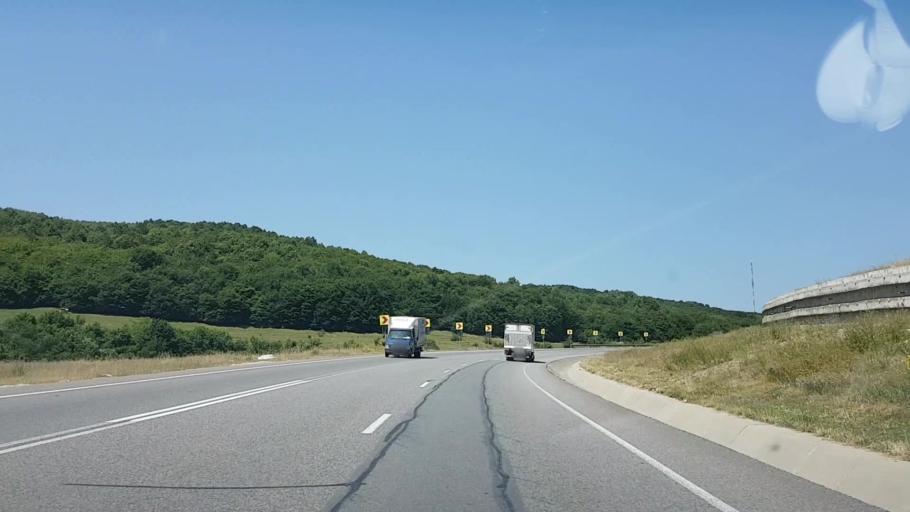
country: RO
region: Cluj
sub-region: Comuna Feleacu
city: Feleacu
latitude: 46.6944
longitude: 23.6361
